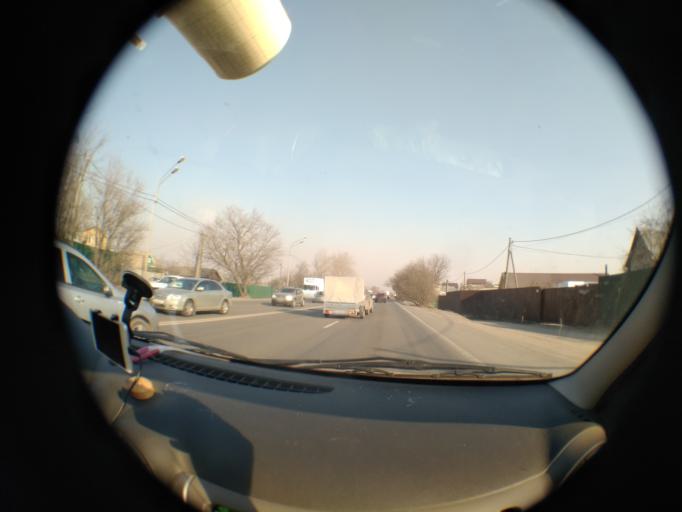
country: RU
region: Moskovskaya
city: Ostrovtsy
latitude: 55.5925
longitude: 38.0004
